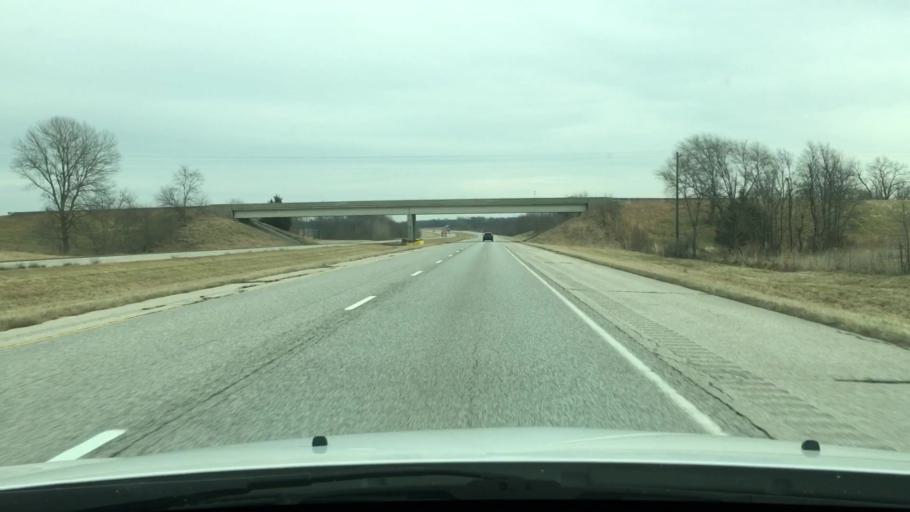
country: US
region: Illinois
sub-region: Pike County
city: Griggsville
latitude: 39.6781
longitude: -90.7055
